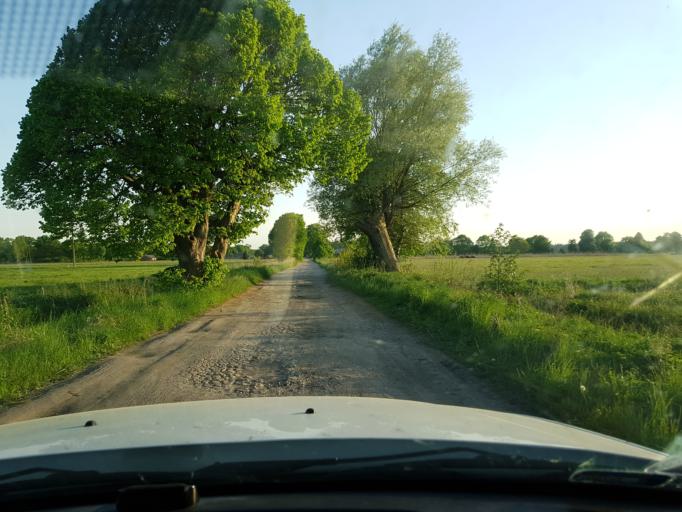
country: PL
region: West Pomeranian Voivodeship
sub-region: Powiat stargardzki
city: Kobylanka
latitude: 53.4026
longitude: 14.8881
